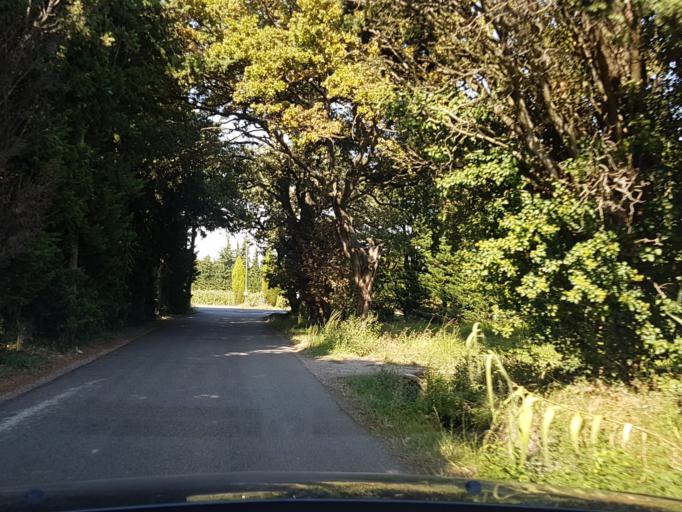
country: FR
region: Provence-Alpes-Cote d'Azur
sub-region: Departement des Bouches-du-Rhone
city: Molleges
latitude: 43.7847
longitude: 4.9220
